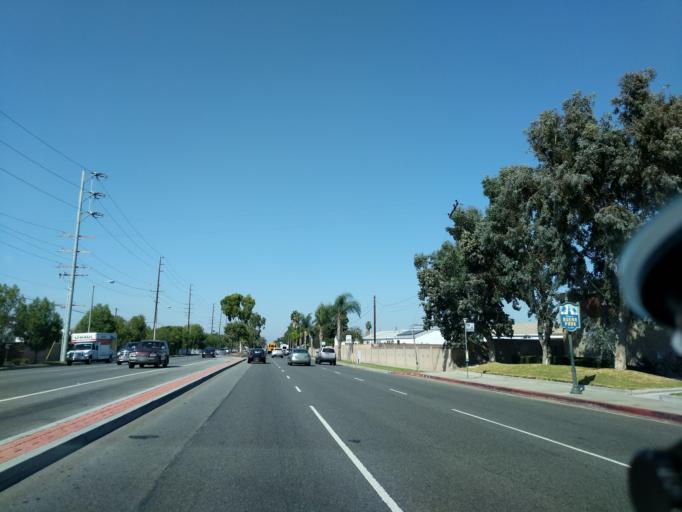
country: US
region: California
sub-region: Orange County
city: Cypress
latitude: 33.8100
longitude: -118.0281
